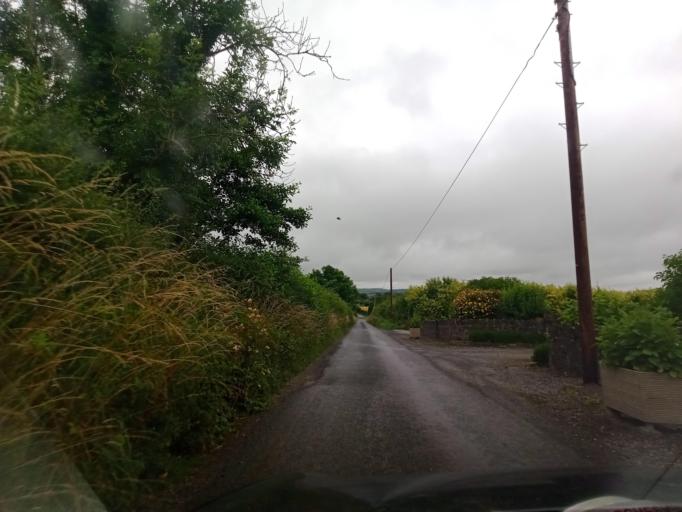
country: IE
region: Leinster
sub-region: Laois
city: Stradbally
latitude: 52.9489
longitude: -7.2322
